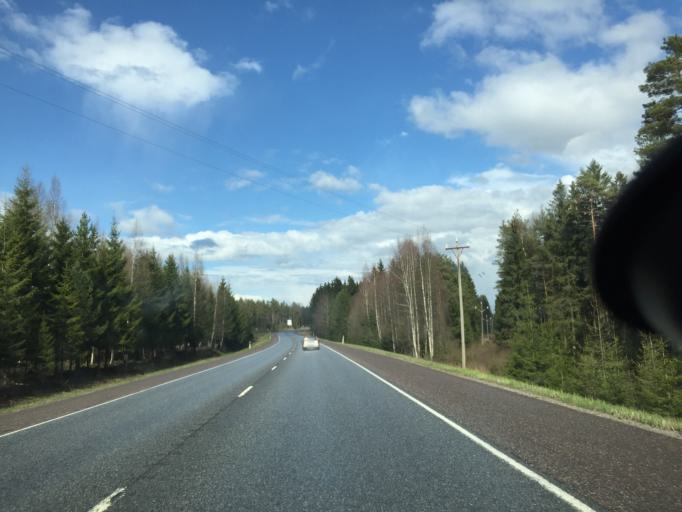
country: FI
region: Uusimaa
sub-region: Raaseporin
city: Karis
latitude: 60.0994
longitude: 23.7699
